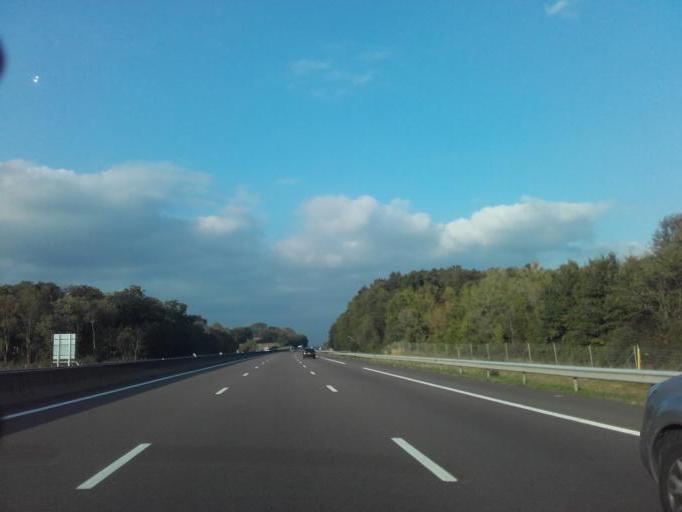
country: FR
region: Bourgogne
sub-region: Departement de Saone-et-Loire
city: Tournus
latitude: 46.5172
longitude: 4.9133
